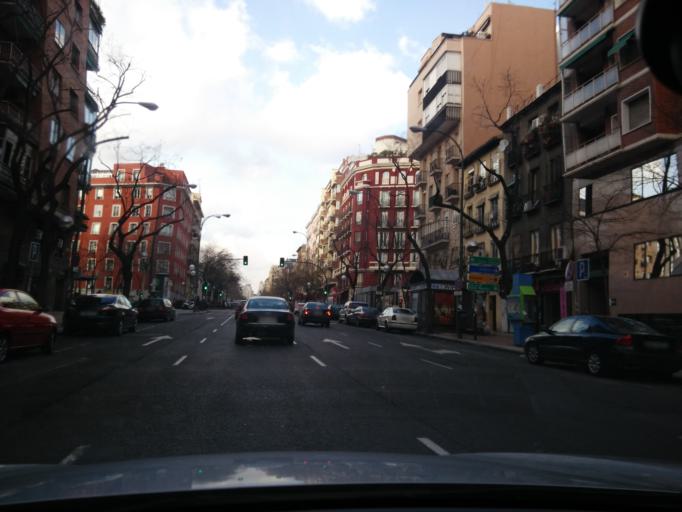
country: ES
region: Madrid
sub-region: Provincia de Madrid
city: Chamberi
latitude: 40.4379
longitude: -3.6998
